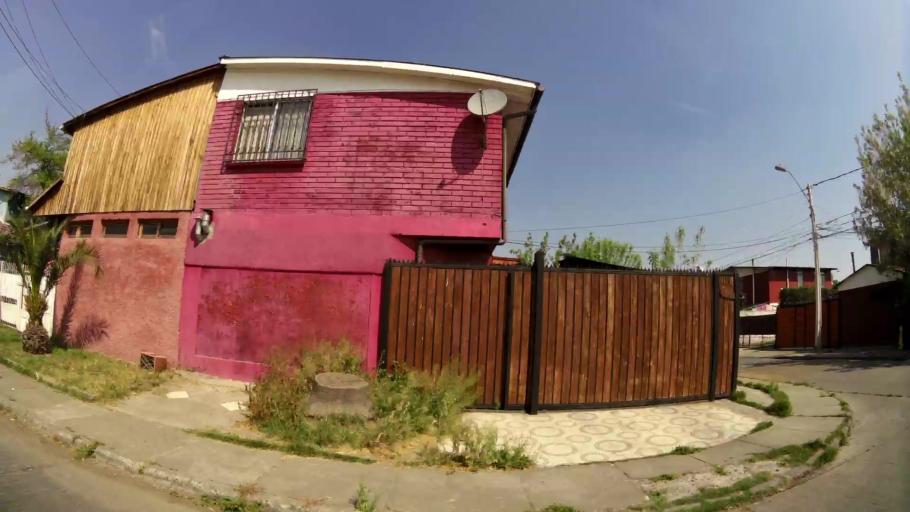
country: CL
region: Santiago Metropolitan
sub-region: Provincia de Santiago
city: La Pintana
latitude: -33.5451
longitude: -70.5994
